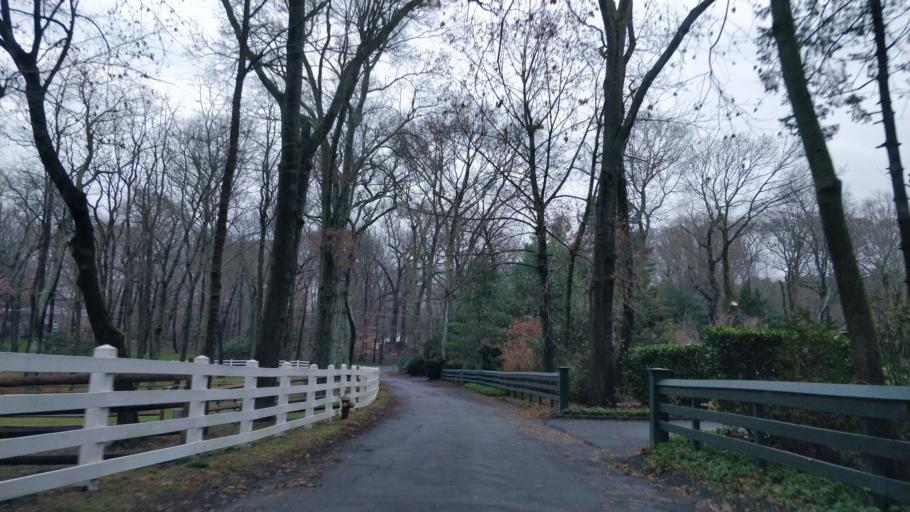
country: US
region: New York
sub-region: Nassau County
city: Upper Brookville
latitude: 40.8589
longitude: -73.5695
